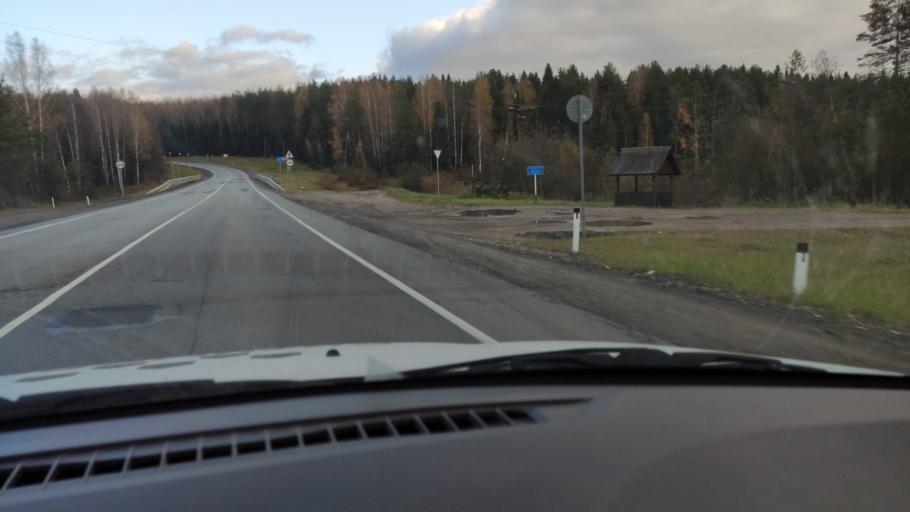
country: RU
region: Kirov
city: Belaya Kholunitsa
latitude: 58.9047
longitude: 50.9465
